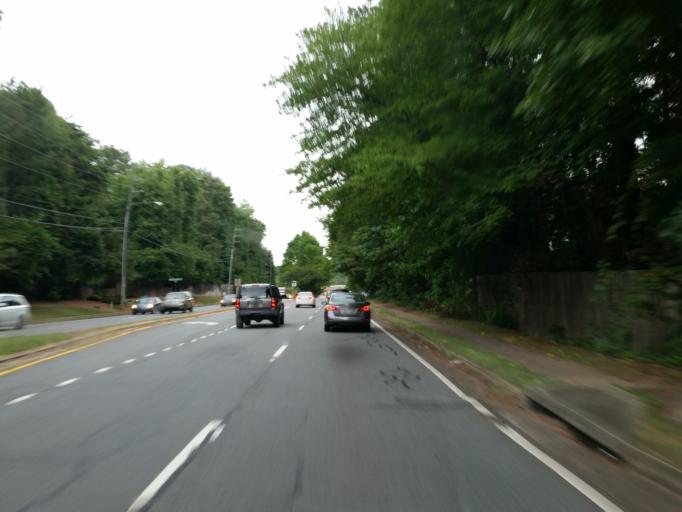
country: US
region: Georgia
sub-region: Fulton County
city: Roswell
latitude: 34.0625
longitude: -84.4289
